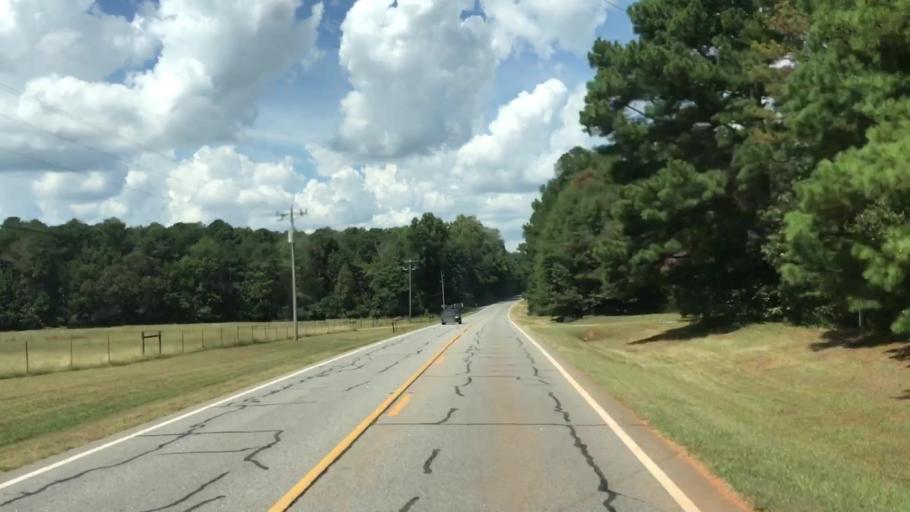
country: US
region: Georgia
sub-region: Oconee County
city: Watkinsville
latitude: 33.8091
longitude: -83.3520
